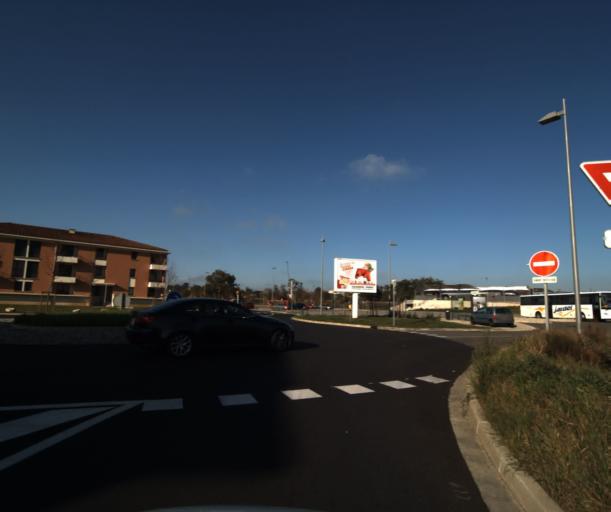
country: FR
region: Midi-Pyrenees
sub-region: Departement de la Haute-Garonne
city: Colomiers
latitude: 43.6016
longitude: 1.3536
